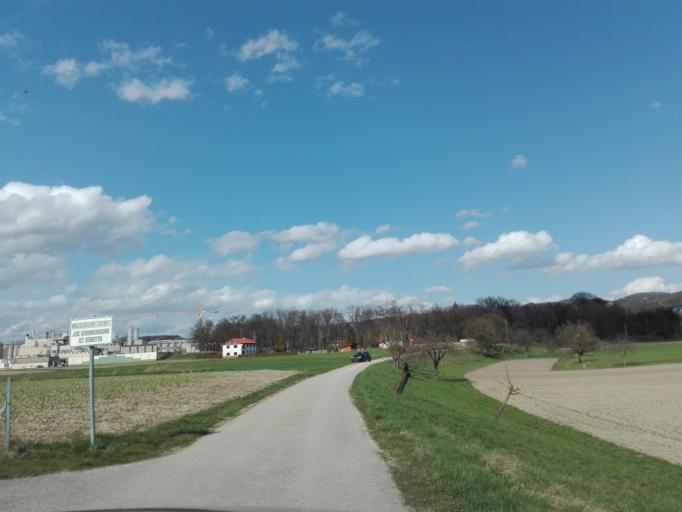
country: AT
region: Upper Austria
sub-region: Politischer Bezirk Urfahr-Umgebung
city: Feldkirchen an der Donau
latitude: 48.3574
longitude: 14.0155
